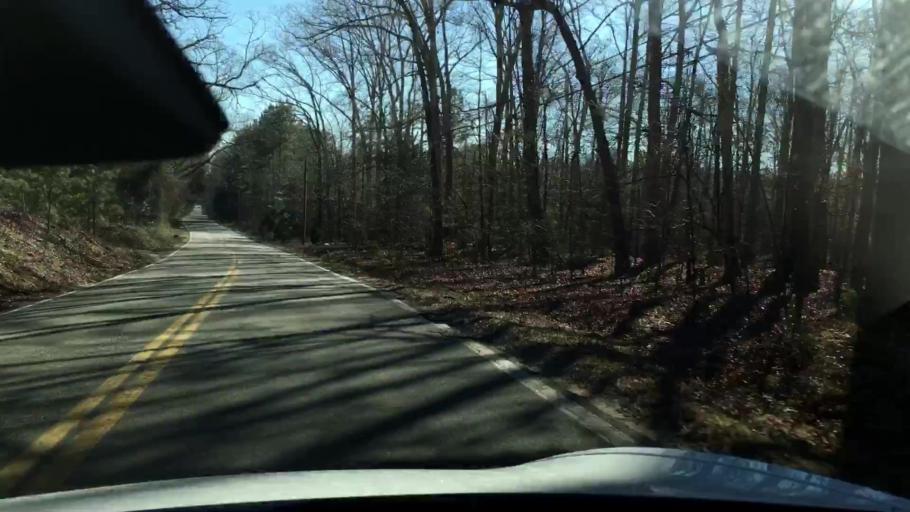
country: US
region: Virginia
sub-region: Henrico County
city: Short Pump
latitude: 37.5848
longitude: -77.7480
